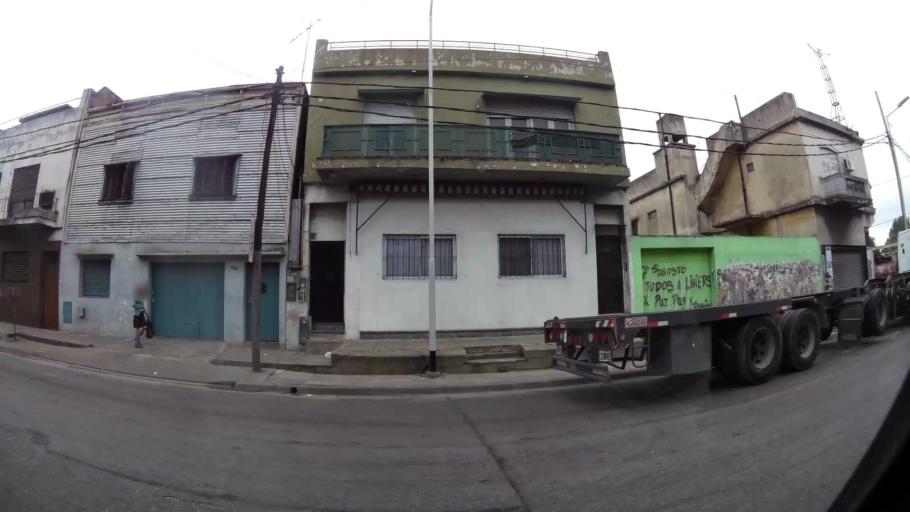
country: AR
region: Buenos Aires
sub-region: Partido de Avellaneda
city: Avellaneda
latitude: -34.6480
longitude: -58.3477
